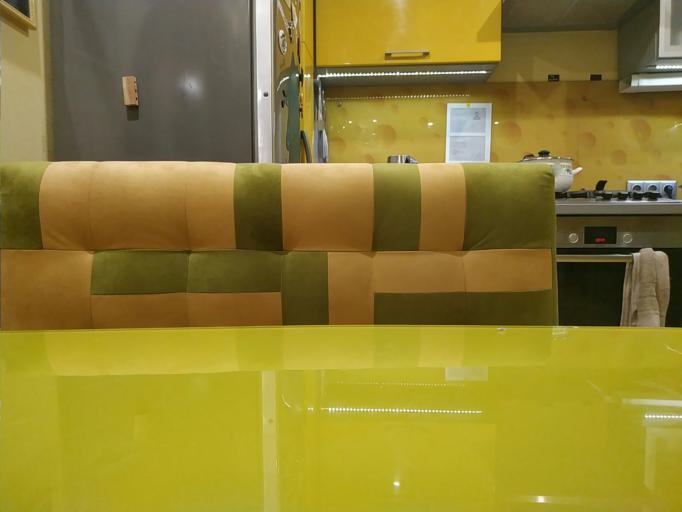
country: RU
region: Murmansk
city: Alakurtti
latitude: 66.2559
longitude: 30.2646
